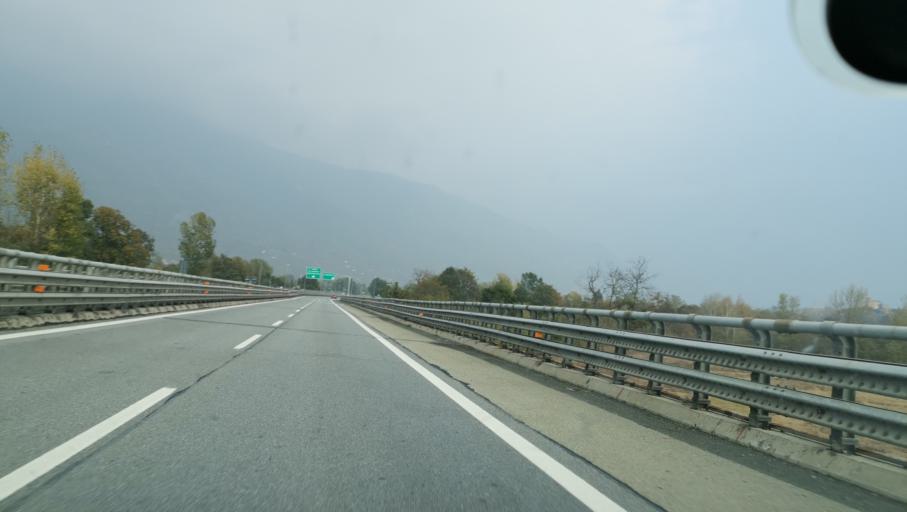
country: IT
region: Piedmont
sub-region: Provincia di Torino
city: San Giorio
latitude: 45.1336
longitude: 7.1672
